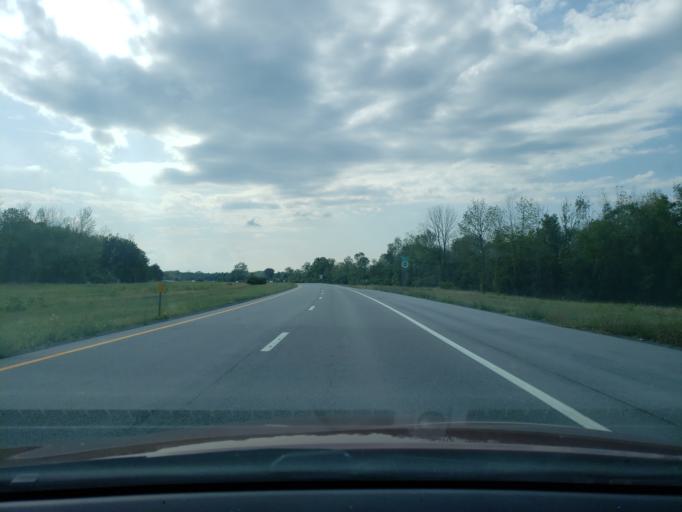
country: US
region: New York
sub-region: Monroe County
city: Greece
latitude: 43.2728
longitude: -77.6718
